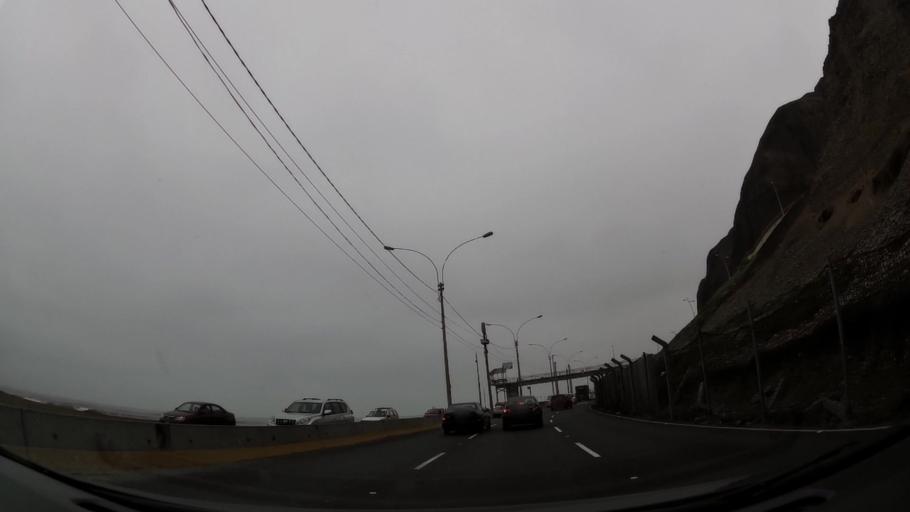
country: PE
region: Lima
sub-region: Lima
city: San Isidro
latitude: -12.1176
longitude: -77.0486
